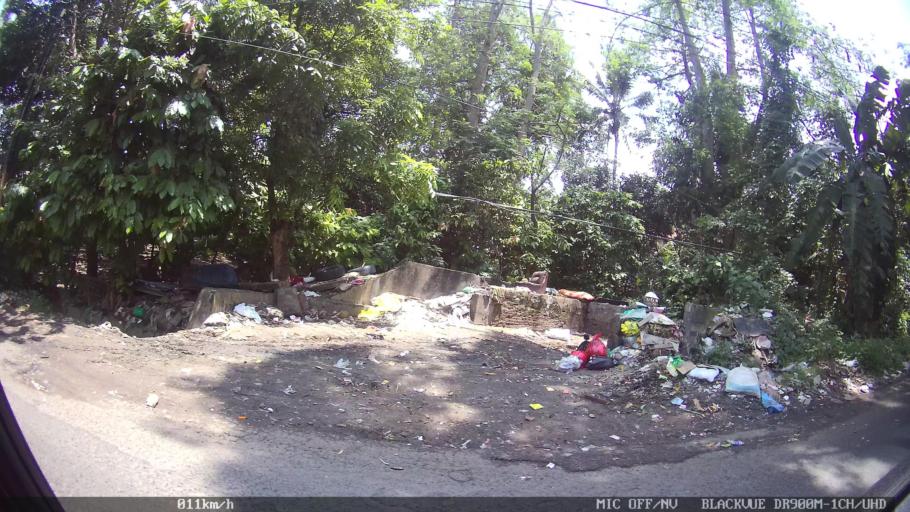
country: ID
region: Lampung
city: Kedaton
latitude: -5.4009
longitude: 105.2539
